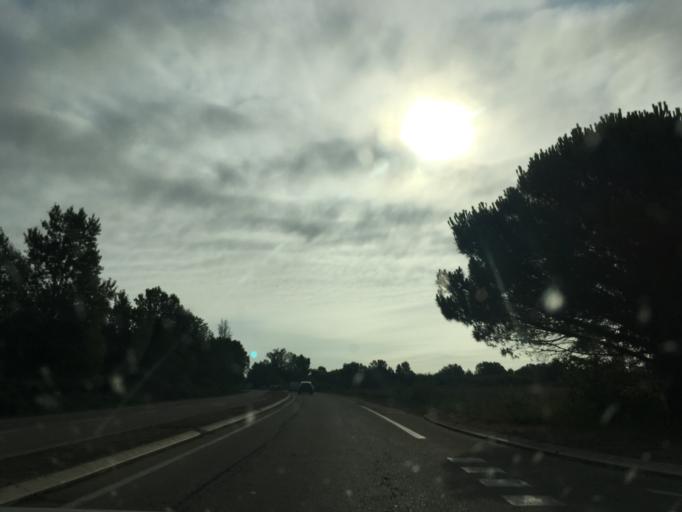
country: FR
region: Languedoc-Roussillon
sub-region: Departement du Gard
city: Saint-Gilles
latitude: 43.5822
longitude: 4.4494
